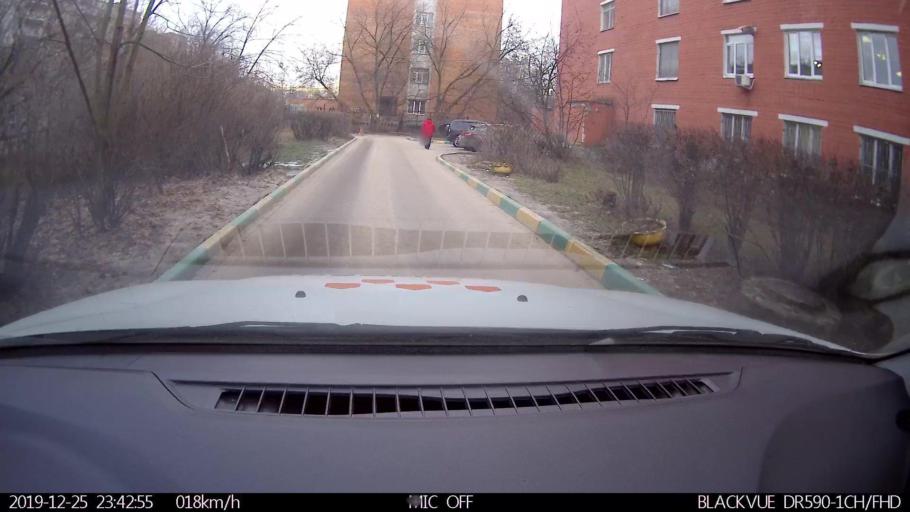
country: RU
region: Nizjnij Novgorod
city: Neklyudovo
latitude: 56.3476
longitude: 43.8612
